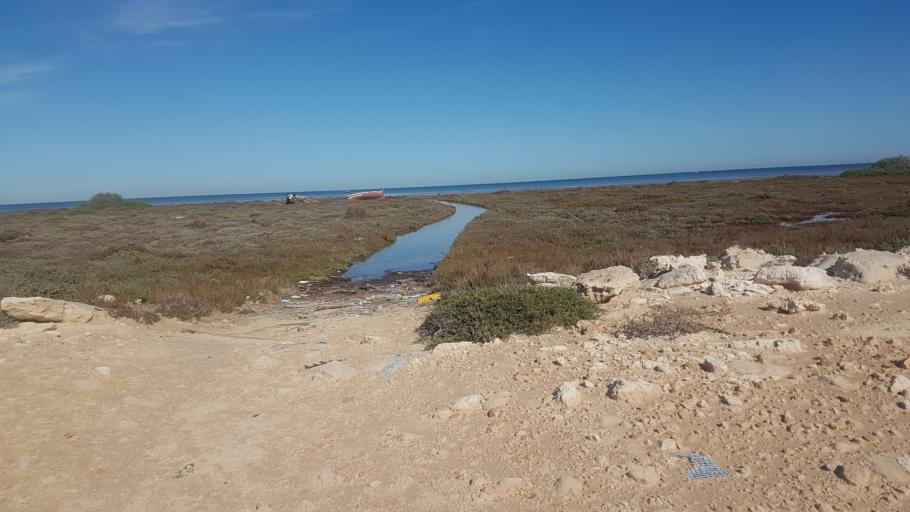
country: TN
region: Safaqis
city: Al Qarmadah
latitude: 34.6676
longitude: 11.0482
